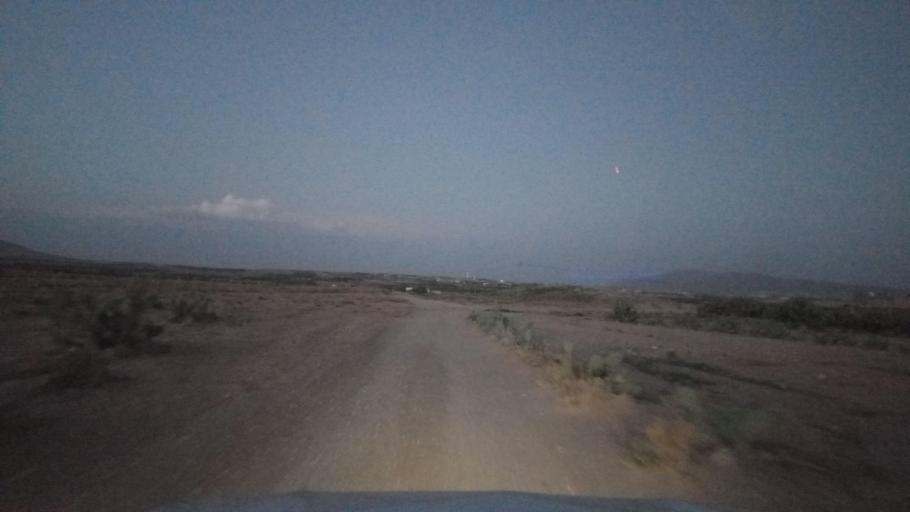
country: TN
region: Al Qasrayn
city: Sbiba
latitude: 35.3791
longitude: 9.0253
